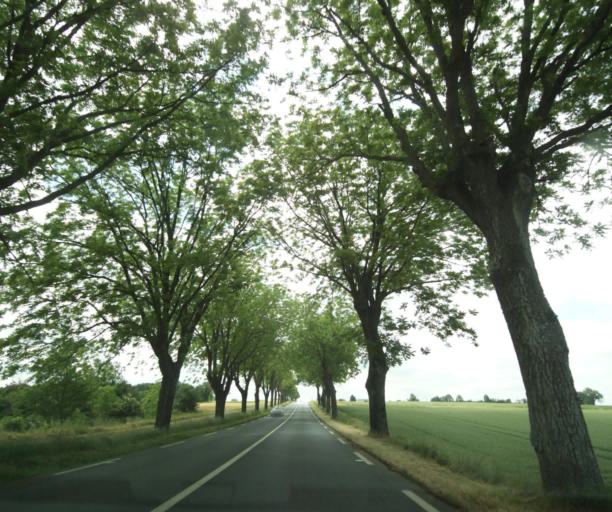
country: FR
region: Poitou-Charentes
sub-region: Departement des Deux-Sevres
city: Saint-Jean-de-Thouars
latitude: 46.9299
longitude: -0.1995
